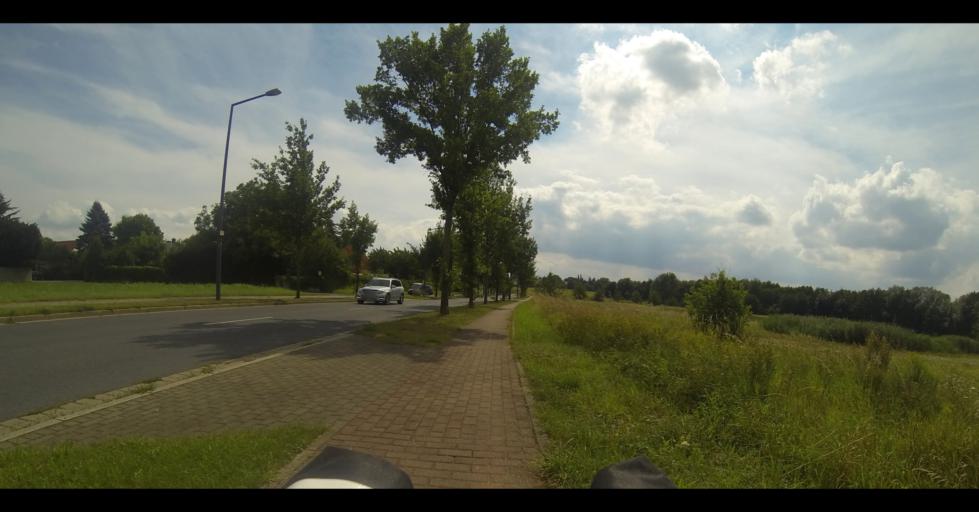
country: DE
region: Saxony
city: Albertstadt
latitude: 51.1223
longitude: 13.7316
